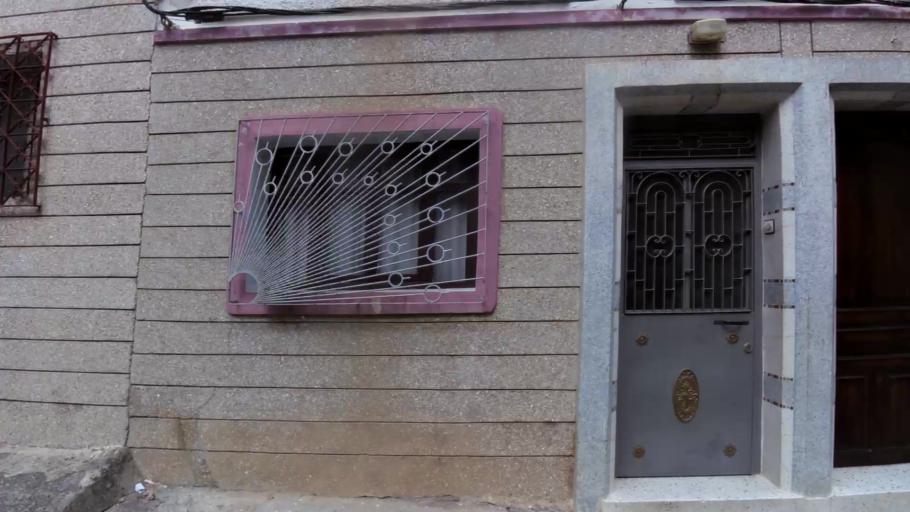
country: MA
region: Tanger-Tetouan
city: Tetouan
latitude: 35.5812
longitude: -5.3589
